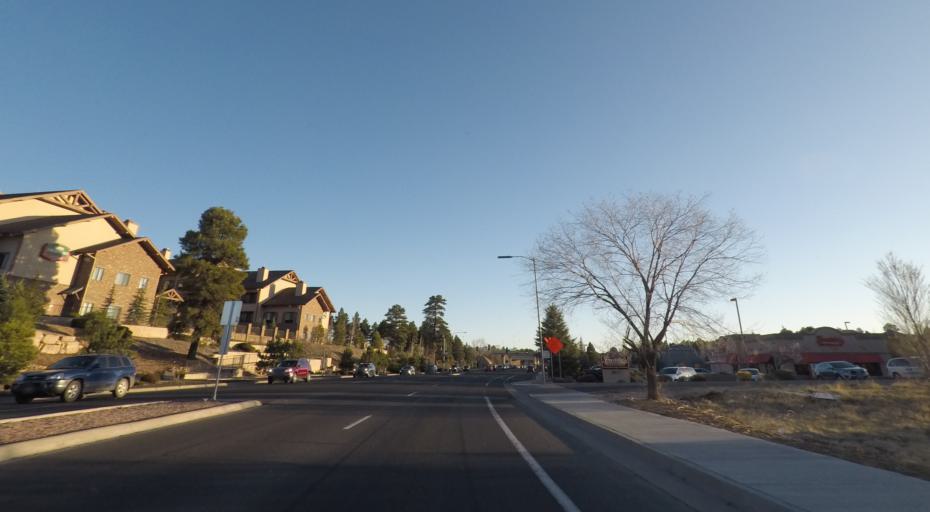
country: US
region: Arizona
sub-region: Coconino County
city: Flagstaff
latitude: 35.1756
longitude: -111.6633
